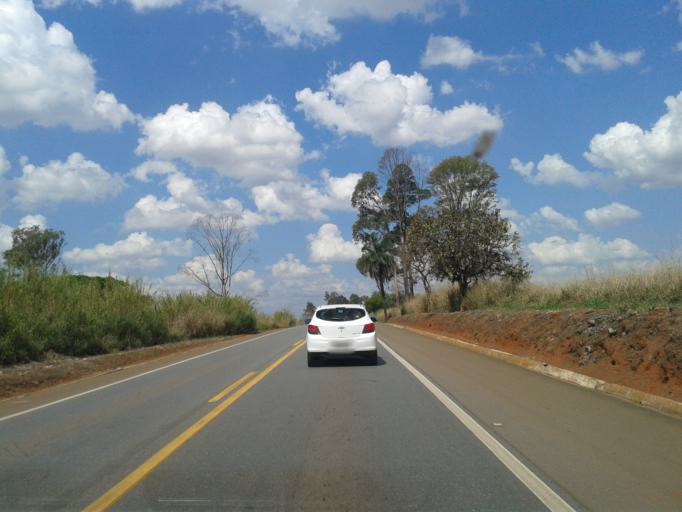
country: BR
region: Minas Gerais
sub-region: Luz
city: Luz
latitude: -19.7748
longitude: -45.7586
